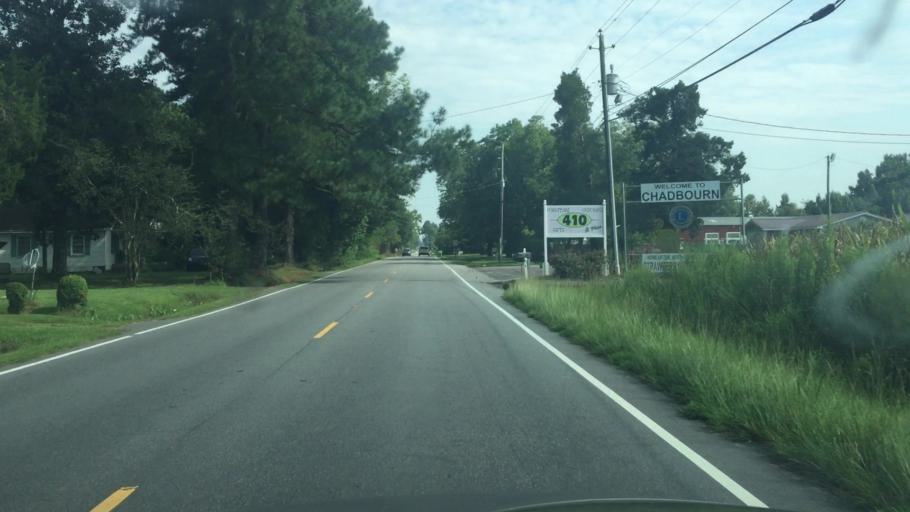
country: US
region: North Carolina
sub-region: Columbus County
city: Chadbourn
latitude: 34.3099
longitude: -78.8264
